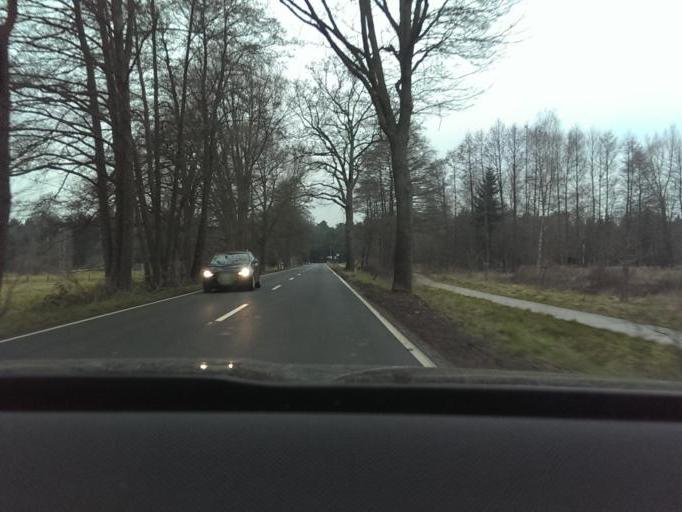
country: DE
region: Lower Saxony
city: Isernhagen Farster Bauerschaft
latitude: 52.5157
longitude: 9.8004
